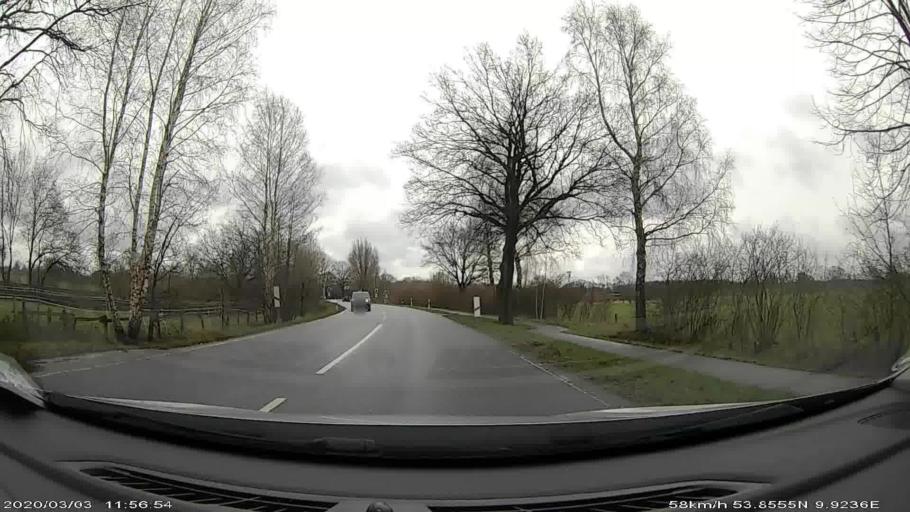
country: DE
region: Schleswig-Holstein
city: Nutzen
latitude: 53.8548
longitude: 9.9264
